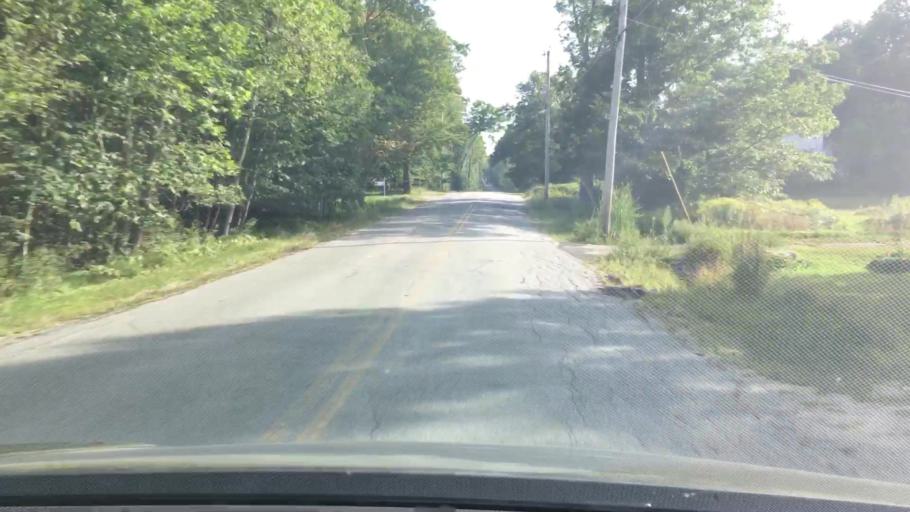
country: US
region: Maine
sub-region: Hancock County
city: Bucksport
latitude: 44.5549
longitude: -68.7950
